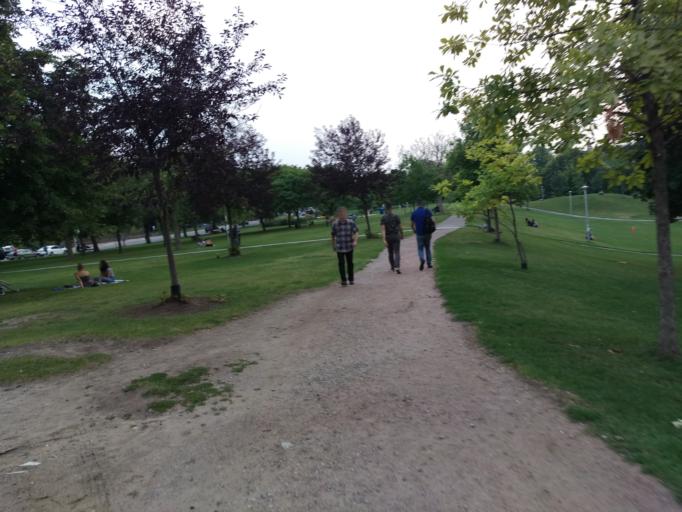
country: CA
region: Ontario
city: Toronto
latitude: 43.6640
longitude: -79.4190
